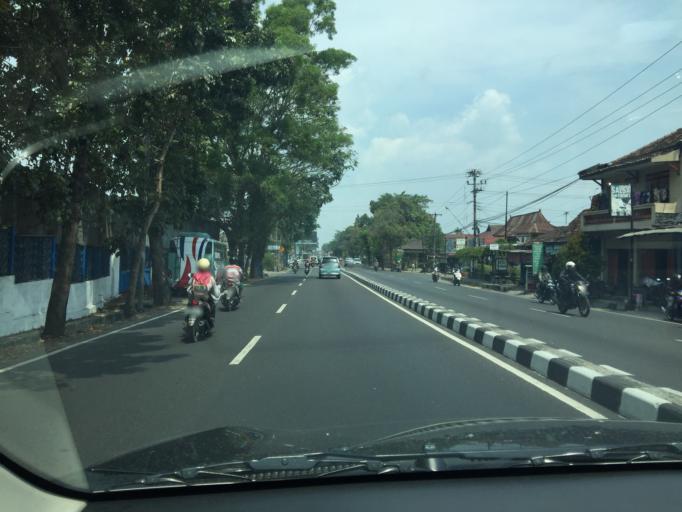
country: ID
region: Daerah Istimewa Yogyakarta
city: Sleman
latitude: -7.6817
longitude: 110.3390
